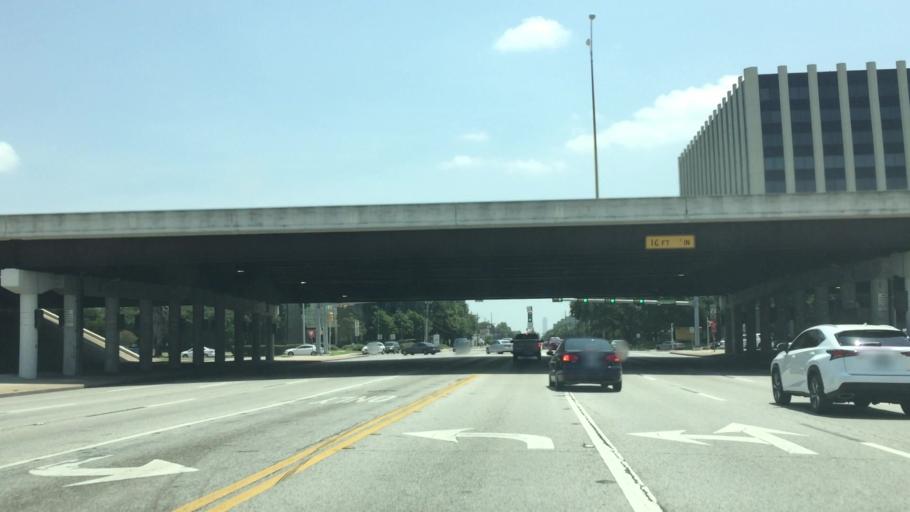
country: US
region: Texas
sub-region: Harris County
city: Bunker Hill Village
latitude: 29.7365
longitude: -95.5571
